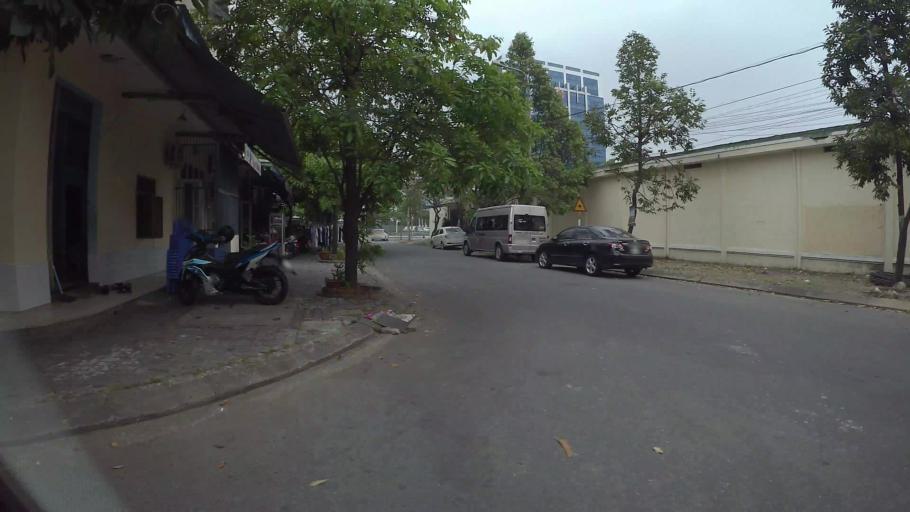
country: VN
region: Da Nang
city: Cam Le
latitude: 16.0356
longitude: 108.2126
